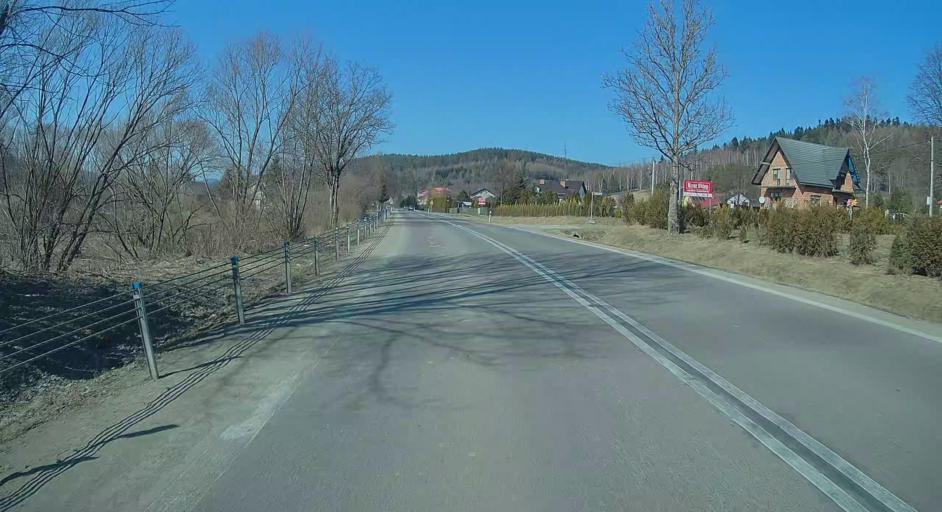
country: PL
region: Subcarpathian Voivodeship
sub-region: Powiat bieszczadzki
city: Ustrzyki Dolne
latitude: 49.5687
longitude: 22.5555
